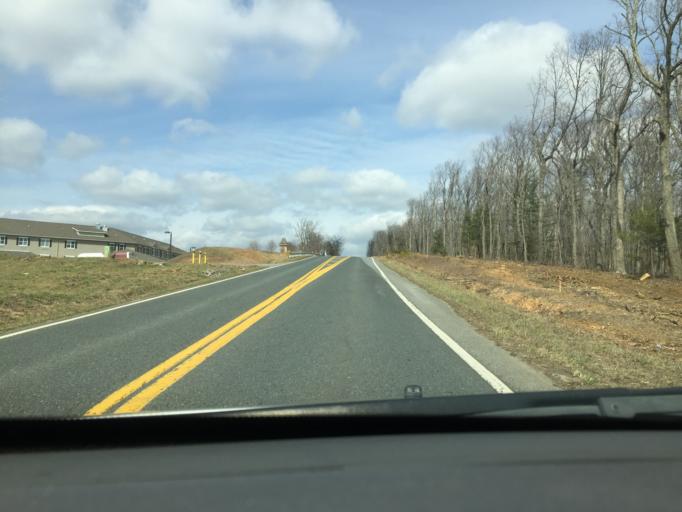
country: US
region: Virginia
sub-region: City of Lynchburg
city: West Lynchburg
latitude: 37.3373
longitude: -79.1718
